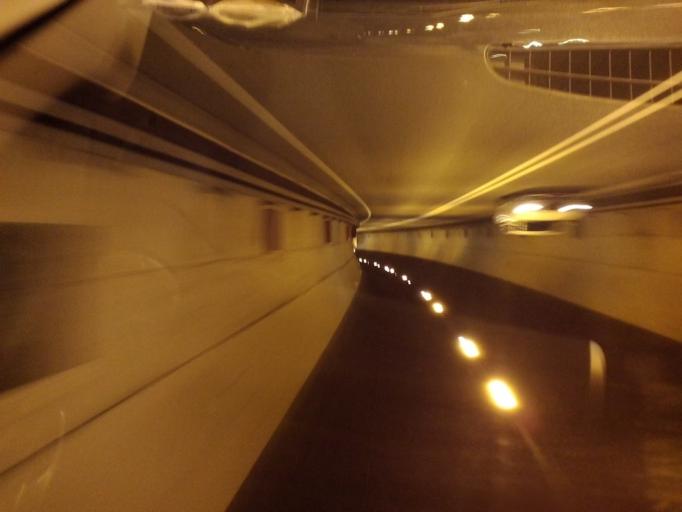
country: IT
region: Trentino-Alto Adige
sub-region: Bolzano
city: Rio di Pusteria
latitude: 46.7950
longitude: 11.6684
